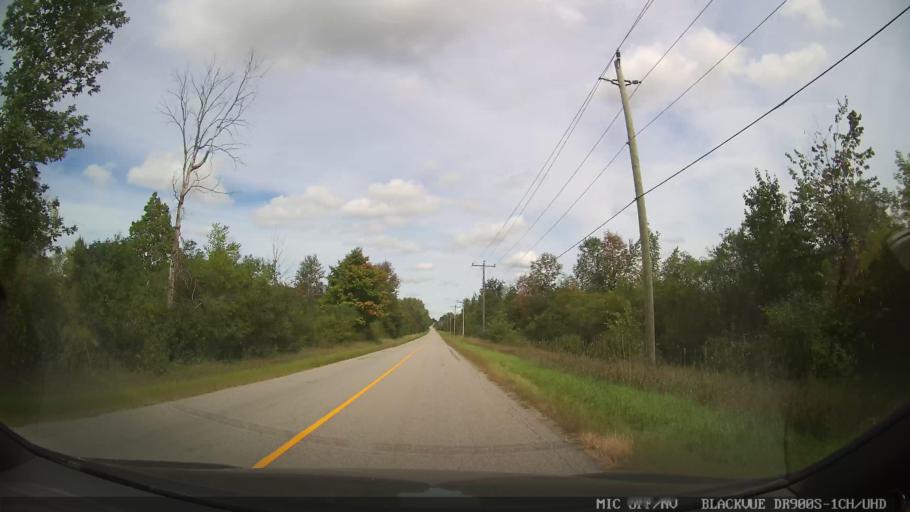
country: CA
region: Ontario
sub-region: Lanark County
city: Smiths Falls
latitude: 44.9102
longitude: -75.8953
